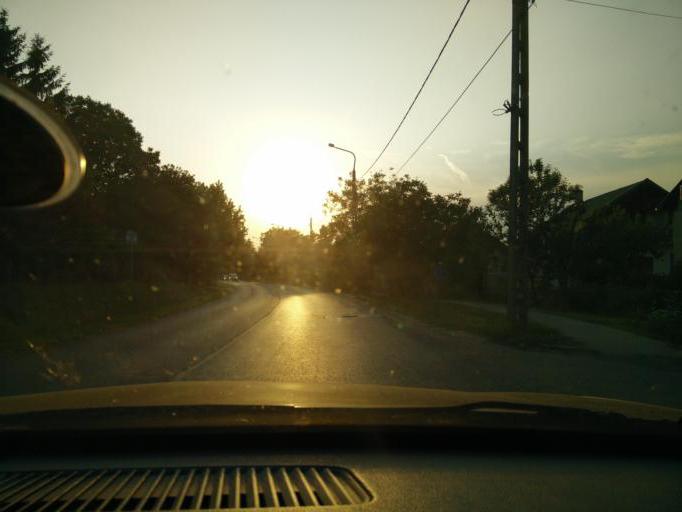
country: HU
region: Pest
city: Toeroekbalint
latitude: 47.4485
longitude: 18.9079
